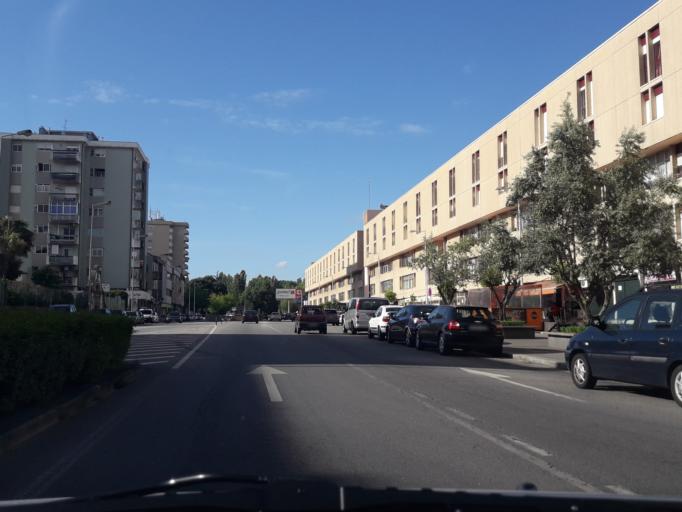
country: PT
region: Braga
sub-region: Vila Nova de Famalicao
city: Vila Nova de Famalicao
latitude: 41.4071
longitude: -8.5165
